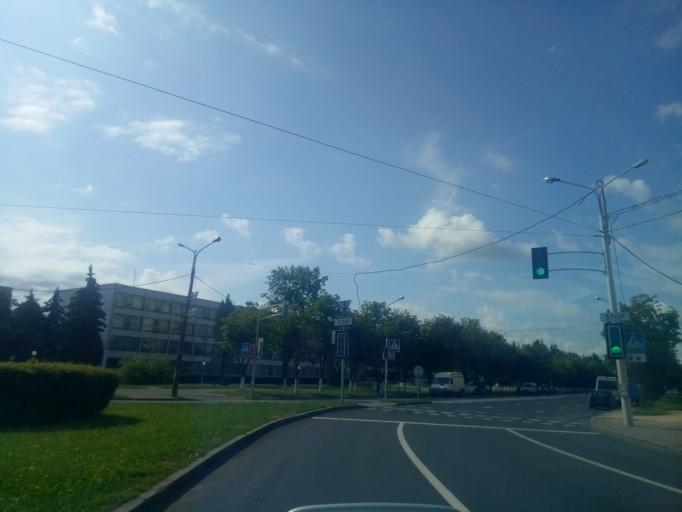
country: BY
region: Minsk
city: Yubilyeyny
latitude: 53.8437
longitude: 27.5054
